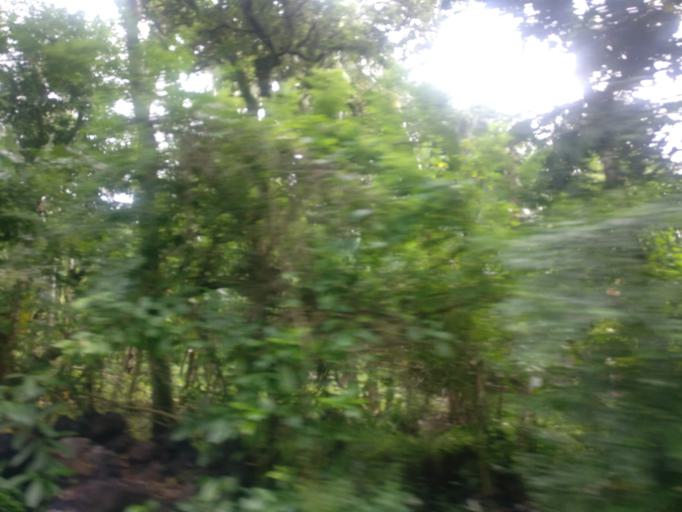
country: ID
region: Bali
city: Banjar Kawan
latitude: -8.4899
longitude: 115.5160
